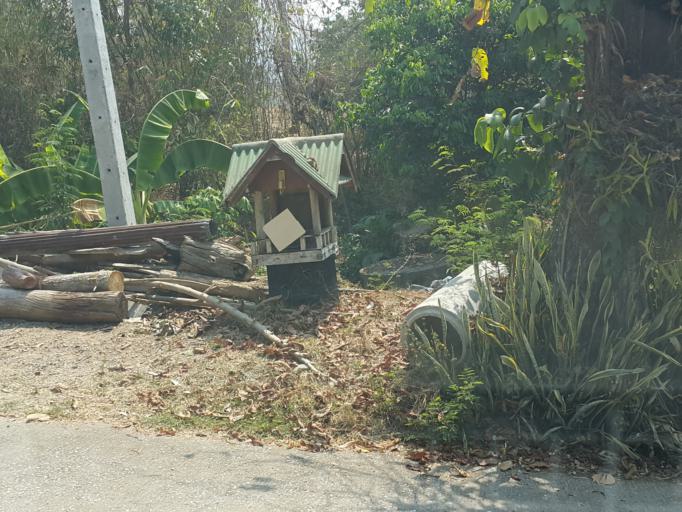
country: TH
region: Chiang Mai
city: Hang Dong
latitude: 18.7722
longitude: 98.8648
